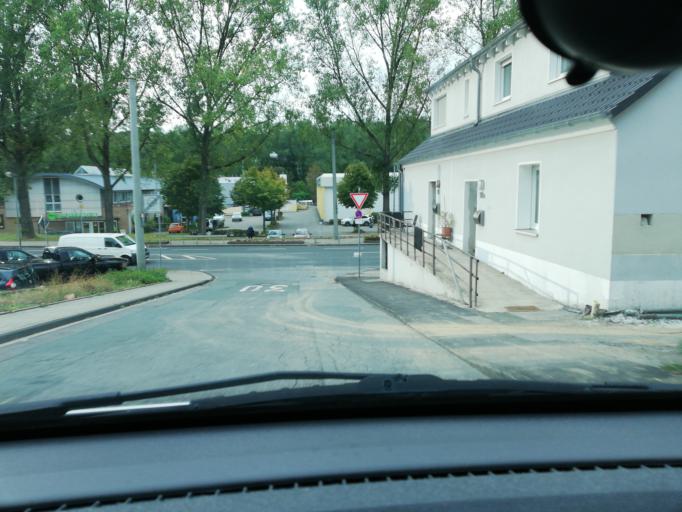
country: DE
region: North Rhine-Westphalia
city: Gevelsberg
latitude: 51.3253
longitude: 7.3543
